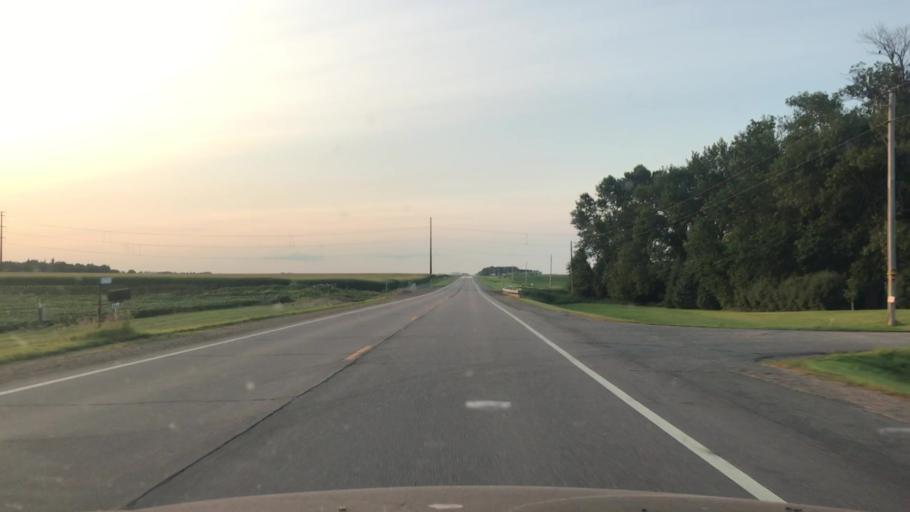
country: US
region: Minnesota
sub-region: Redwood County
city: Redwood Falls
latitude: 44.4290
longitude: -95.1176
